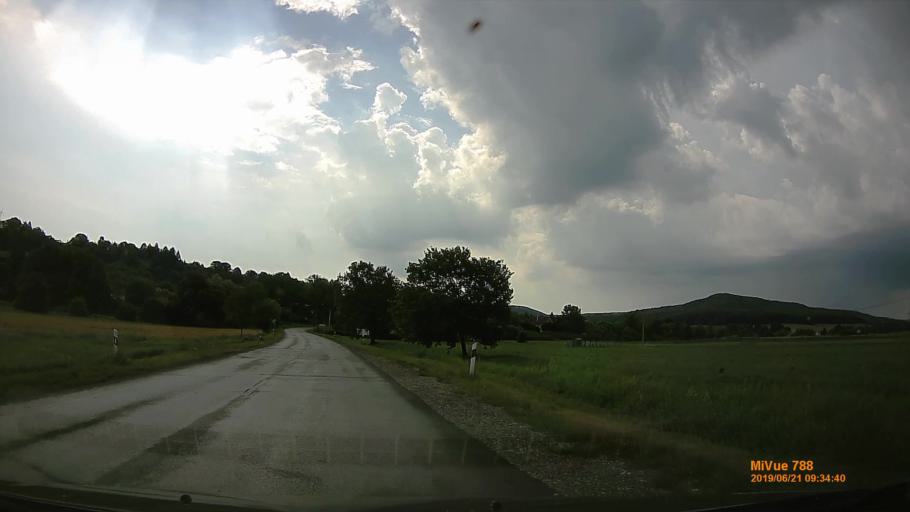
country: HU
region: Somogy
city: Taszar
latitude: 46.3251
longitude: 17.8893
